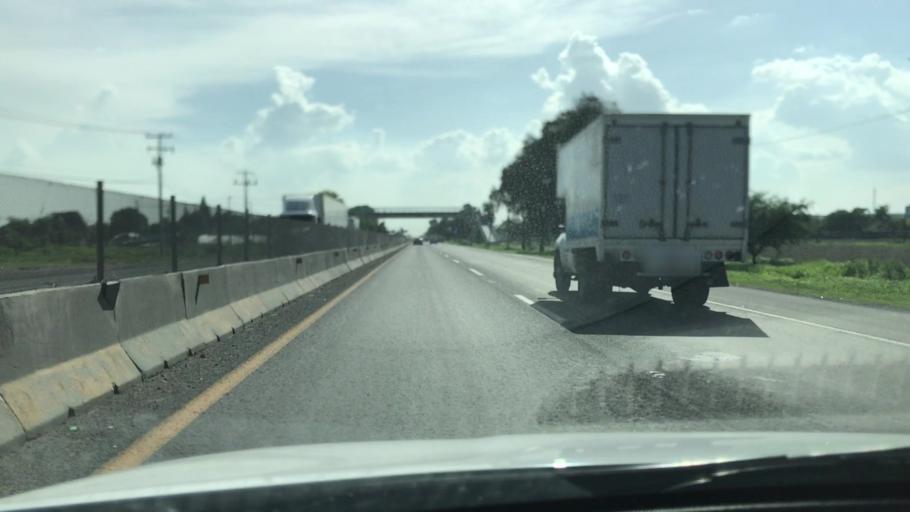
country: MX
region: Guanajuato
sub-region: Villagran
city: El Chinaco (El Pujido)
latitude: 20.5125
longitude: -100.9351
